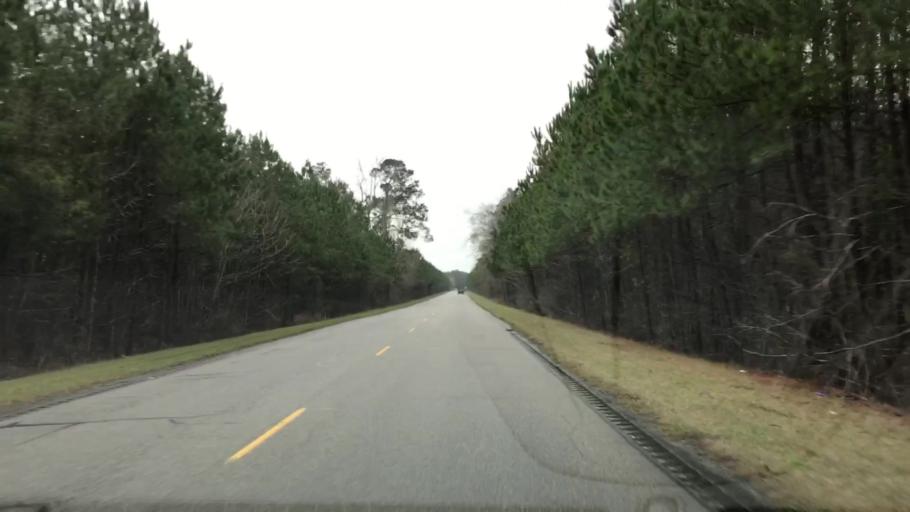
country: US
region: South Carolina
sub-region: Williamsburg County
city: Andrews
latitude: 33.5708
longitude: -79.4513
